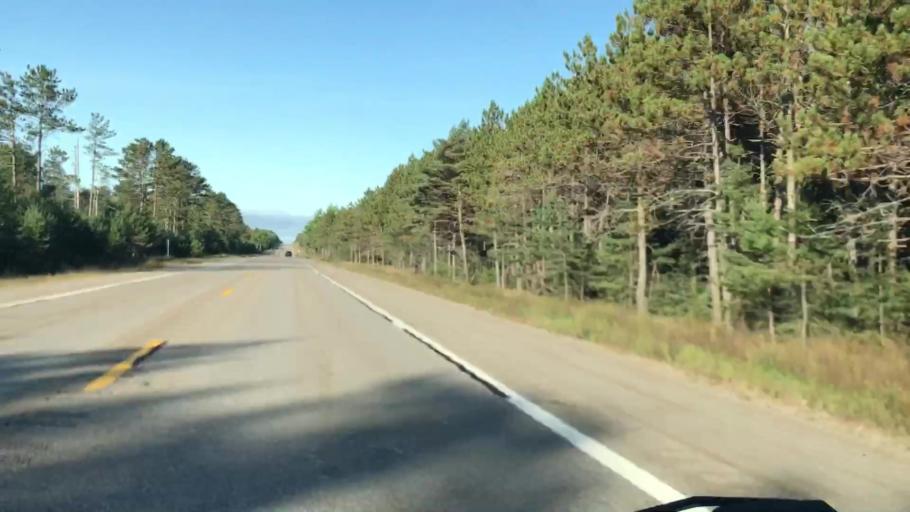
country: US
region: Michigan
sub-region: Chippewa County
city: Sault Ste. Marie
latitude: 46.3676
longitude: -84.7483
